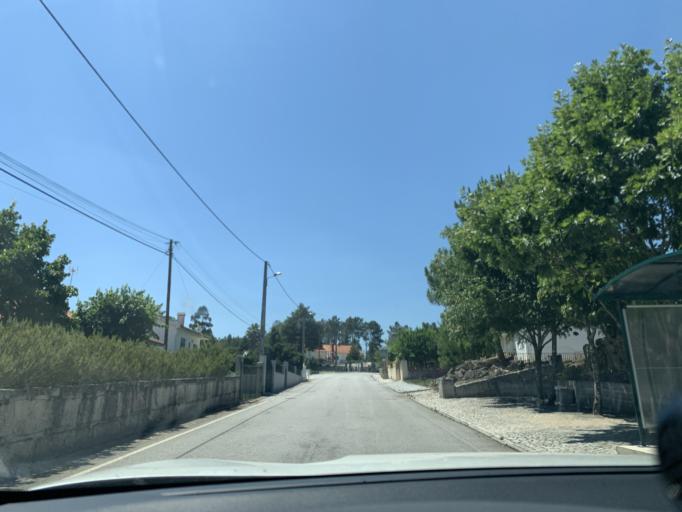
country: PT
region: Viseu
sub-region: Mangualde
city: Mangualde
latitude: 40.5608
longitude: -7.6928
